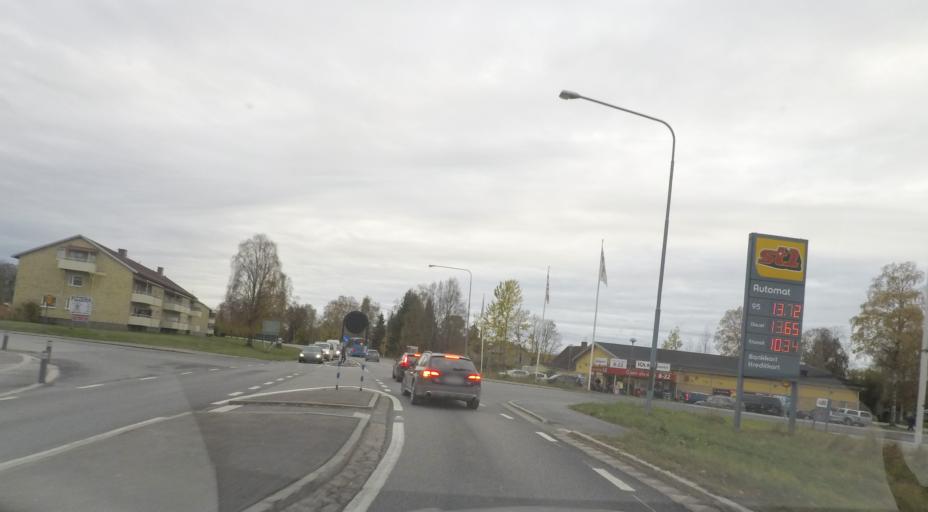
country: SE
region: OErebro
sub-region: Hallefors Kommun
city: Haellefors
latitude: 59.7768
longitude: 14.5252
